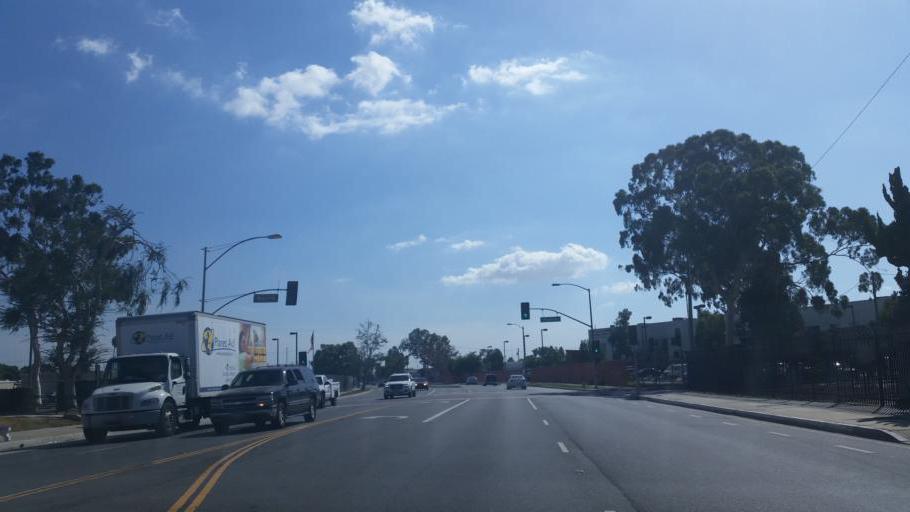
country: US
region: California
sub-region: Los Angeles County
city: Compton
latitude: 33.8929
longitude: -118.2161
